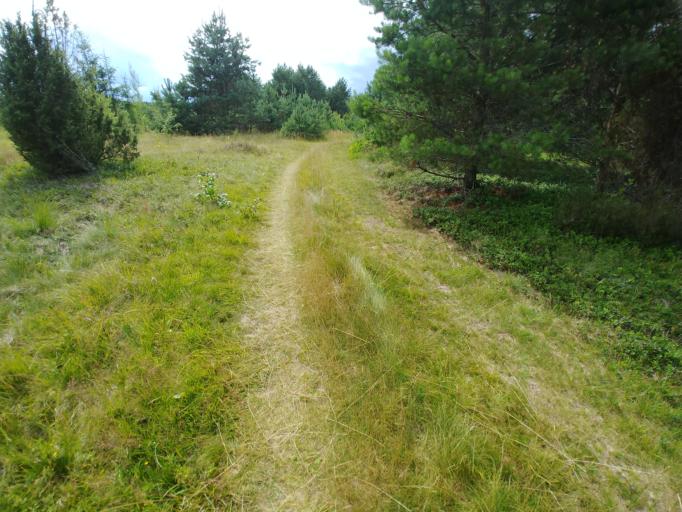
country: BY
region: Vitebsk
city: Byahoml'
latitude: 54.7356
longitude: 28.0440
